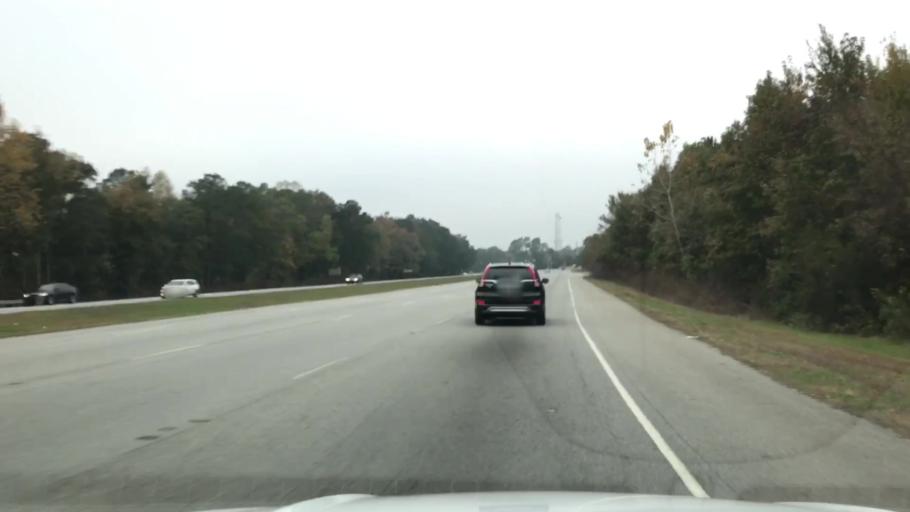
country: US
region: South Carolina
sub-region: Charleston County
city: Shell Point
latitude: 32.8105
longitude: -80.0384
